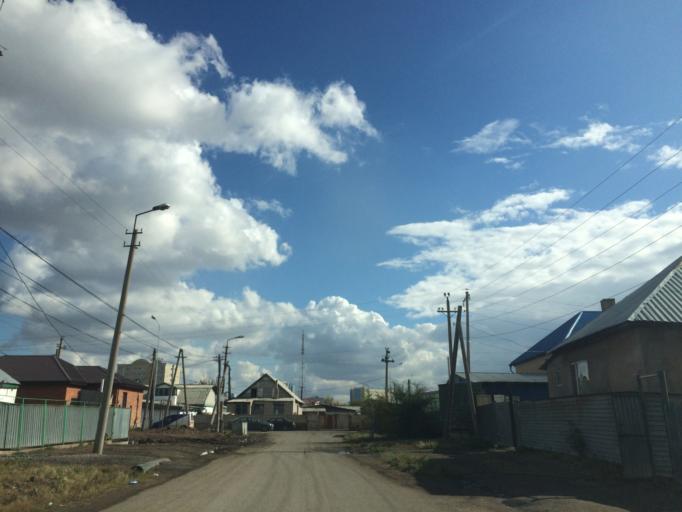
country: KZ
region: Astana Qalasy
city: Astana
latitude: 51.1903
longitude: 71.3956
